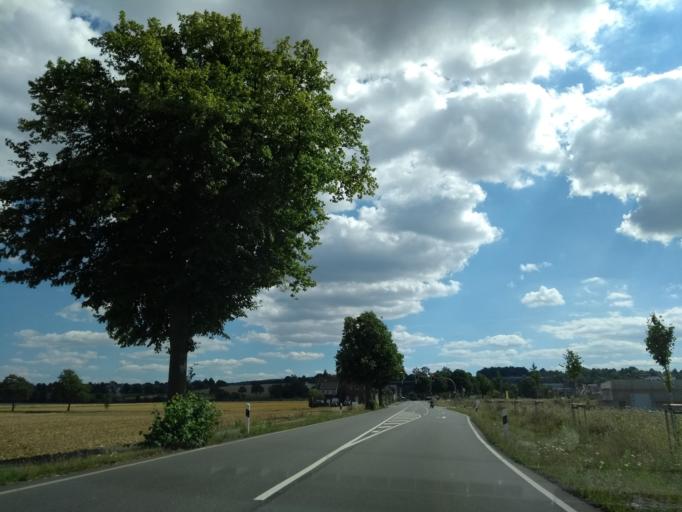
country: DE
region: Lower Saxony
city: Bad Nenndorf
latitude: 52.3452
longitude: 9.3892
